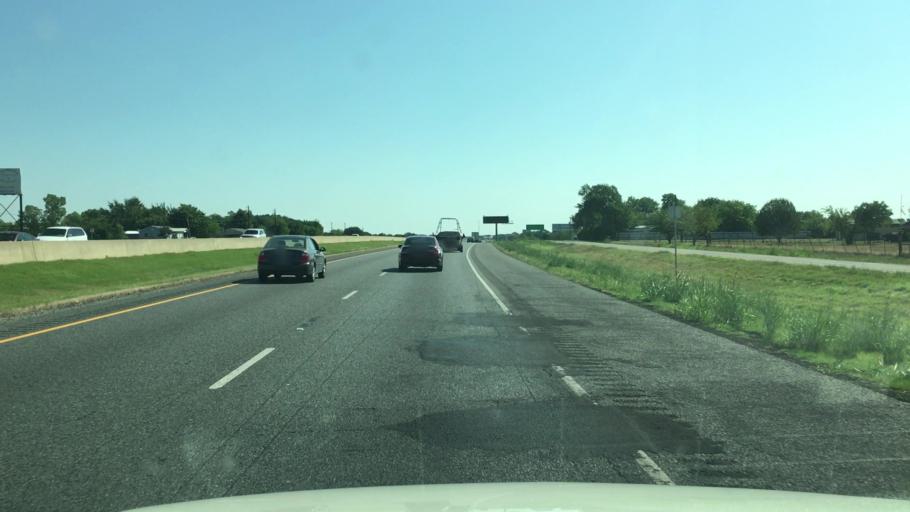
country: US
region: Texas
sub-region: Hunt County
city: Caddo Mills
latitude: 33.0516
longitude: -96.1719
